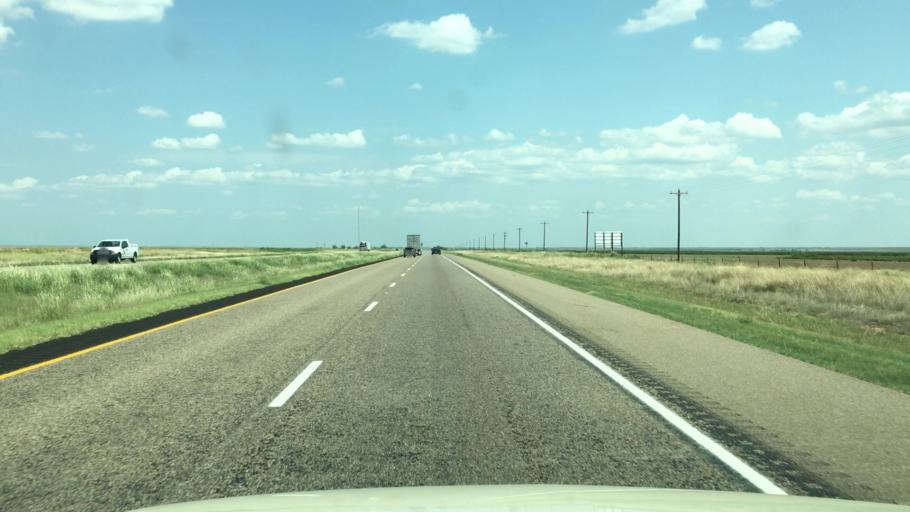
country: US
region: Texas
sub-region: Armstrong County
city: Claude
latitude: 35.0334
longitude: -101.1705
